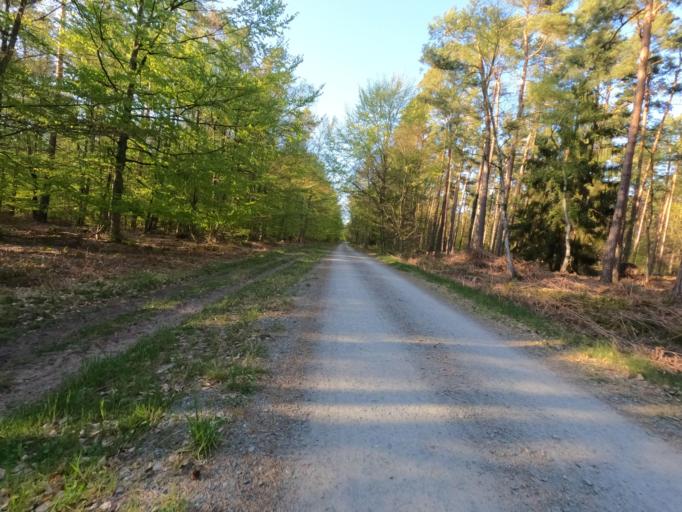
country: DE
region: Mecklenburg-Vorpommern
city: Born
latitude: 54.4162
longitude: 12.5330
